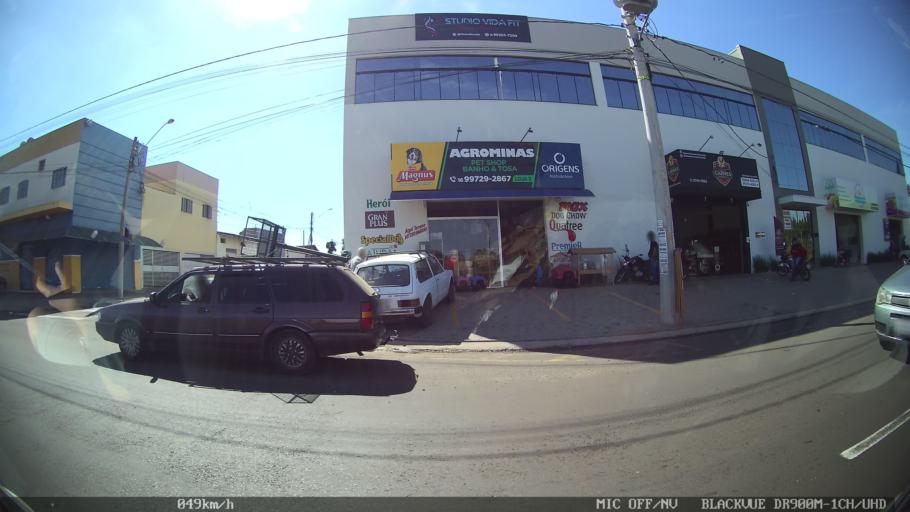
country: BR
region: Sao Paulo
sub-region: Franca
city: Franca
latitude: -20.5462
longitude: -47.4513
